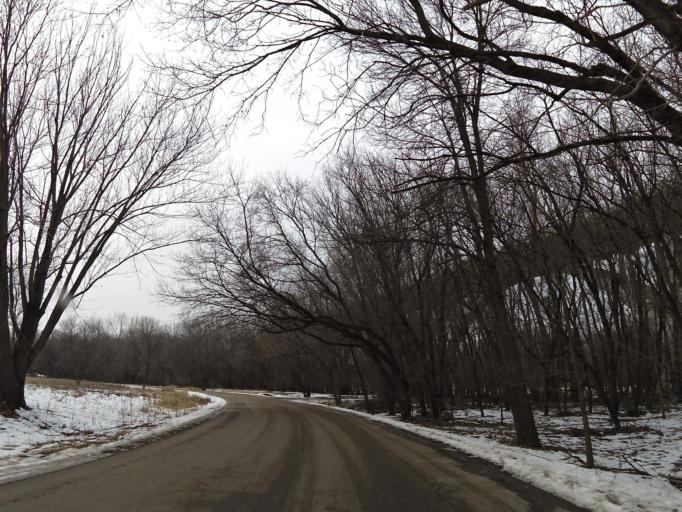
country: US
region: Minnesota
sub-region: Dakota County
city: Mendota Heights
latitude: 44.8854
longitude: -93.1762
